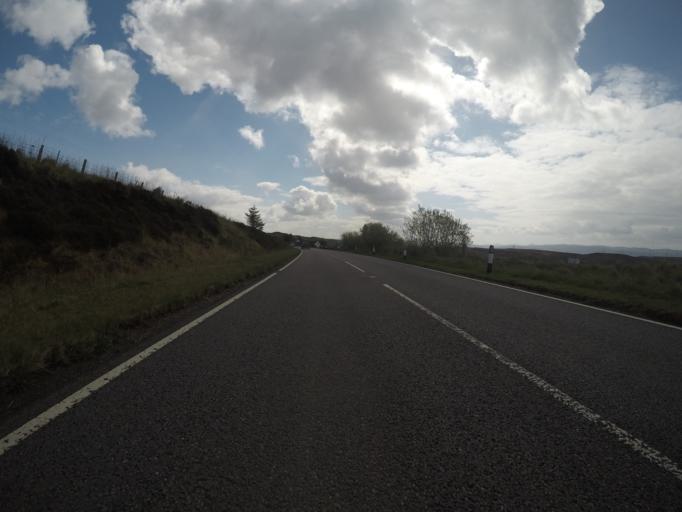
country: GB
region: Scotland
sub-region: Highland
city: Portree
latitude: 57.5630
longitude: -6.3644
